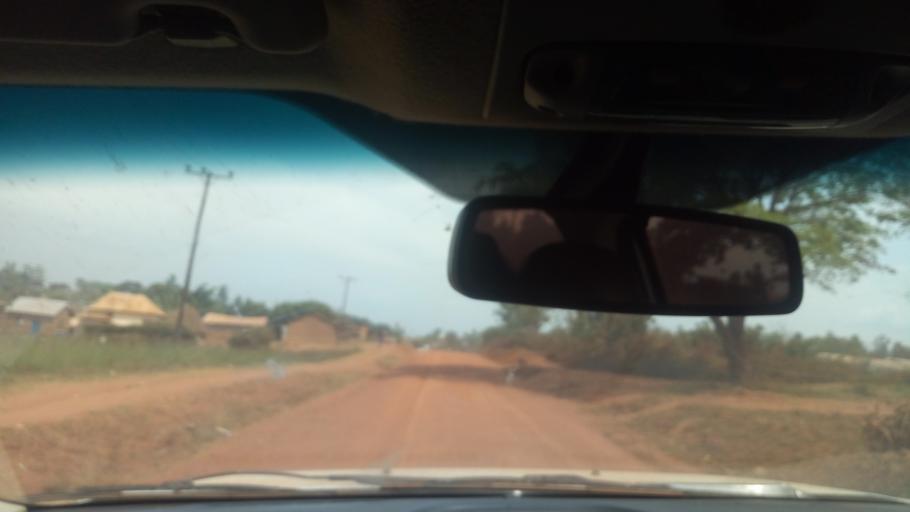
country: UG
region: Western Region
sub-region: Kiryandongo District
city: Kiryandongo
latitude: 1.9412
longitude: 32.1632
